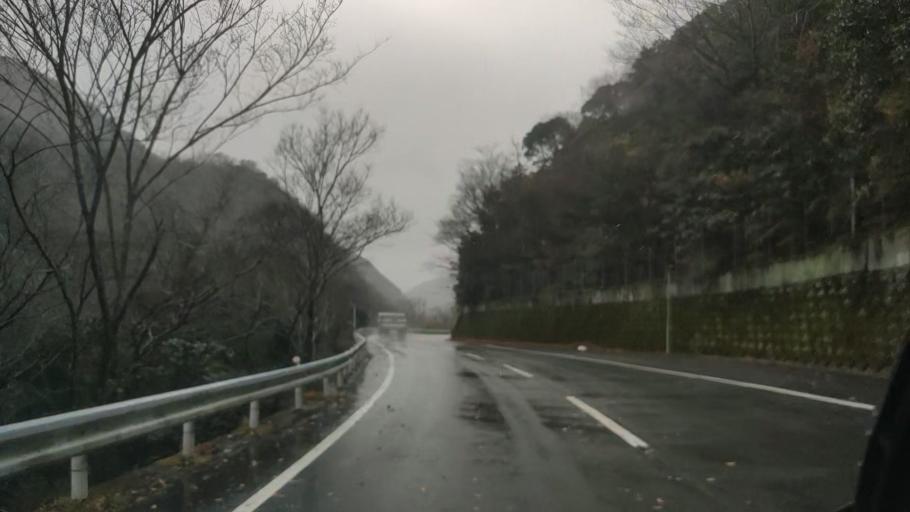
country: JP
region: Tokushima
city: Kamojimacho-jogejima
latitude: 34.1453
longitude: 134.3540
